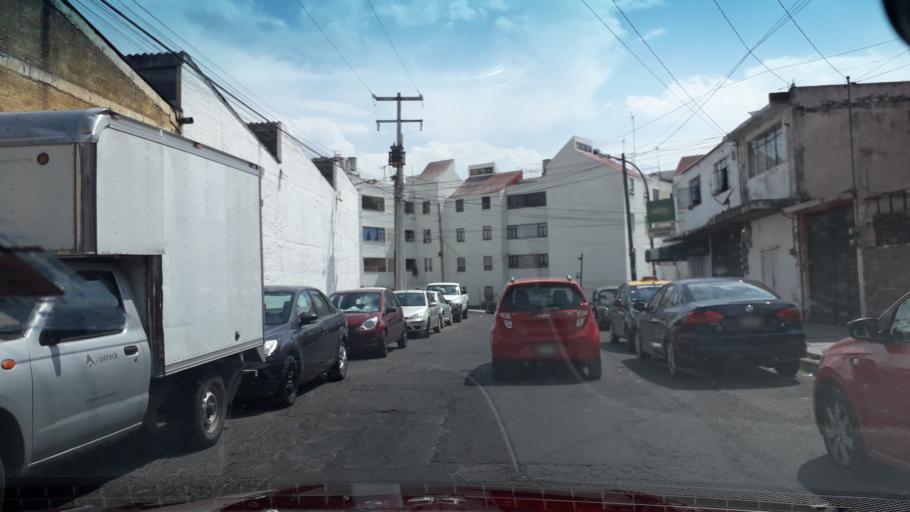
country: MX
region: Puebla
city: Puebla
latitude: 19.0395
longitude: -98.2197
